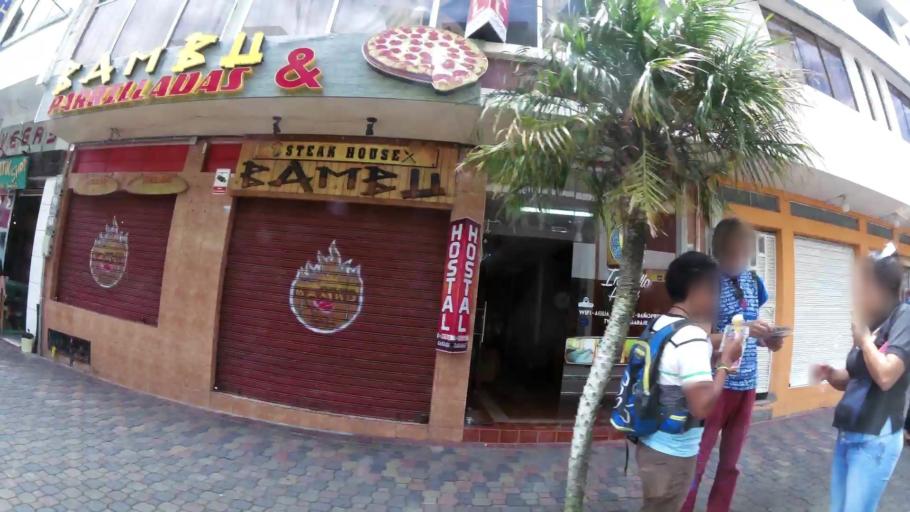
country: EC
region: Tungurahua
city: Banos
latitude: -1.3981
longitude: -78.4219
